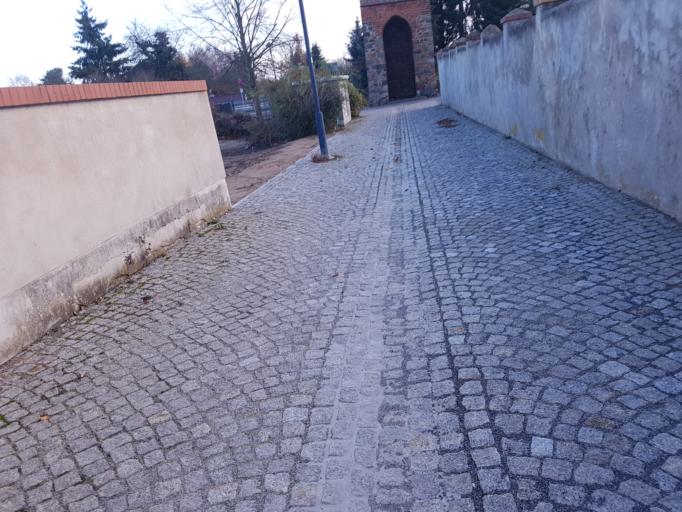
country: DE
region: Brandenburg
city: Juterbog
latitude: 51.9896
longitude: 13.0807
